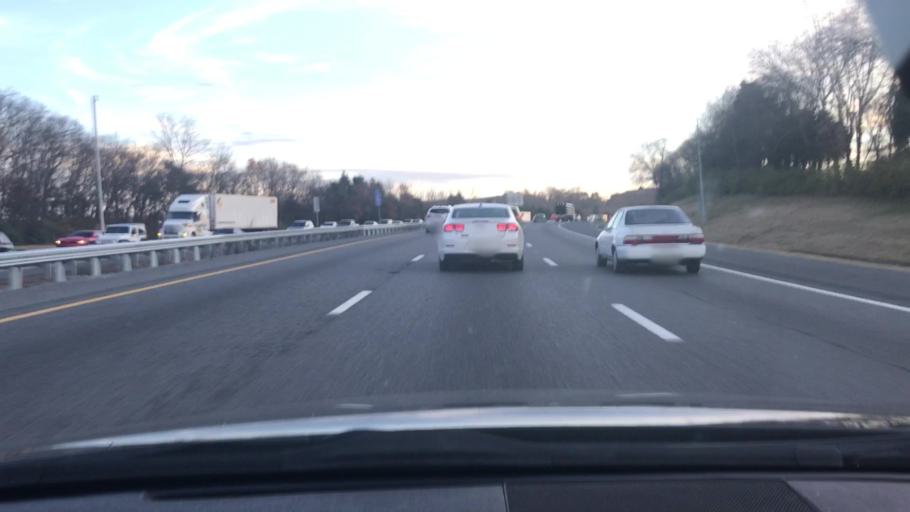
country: US
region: Tennessee
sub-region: Davidson County
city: Goodlettsville
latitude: 36.3166
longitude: -86.7017
